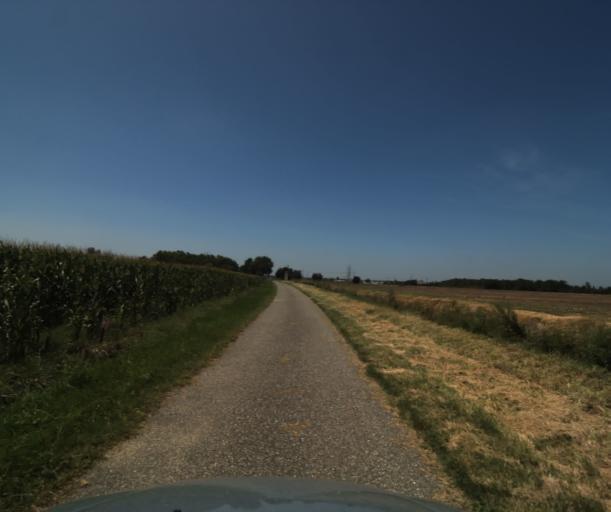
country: FR
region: Midi-Pyrenees
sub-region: Departement de la Haute-Garonne
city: Labastidette
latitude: 43.4620
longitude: 1.2716
